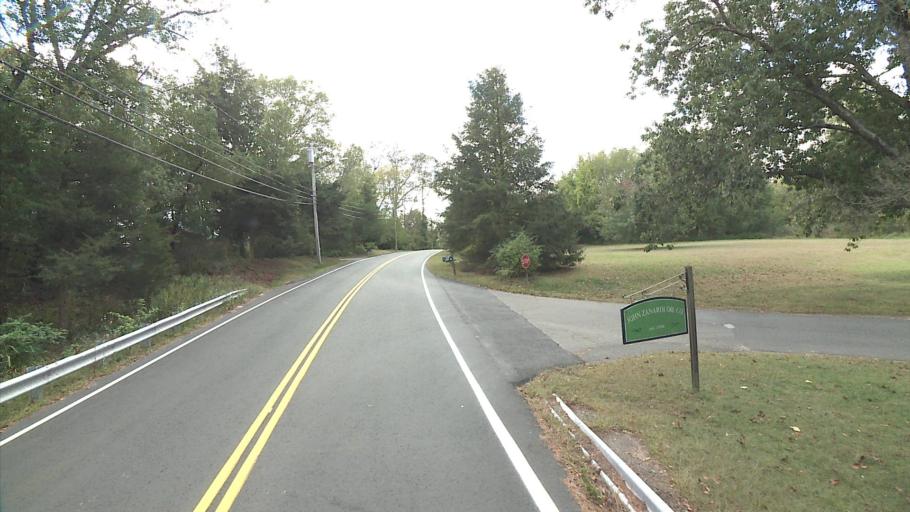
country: US
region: Connecticut
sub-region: Middlesex County
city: Chester Center
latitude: 41.4145
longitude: -72.4376
